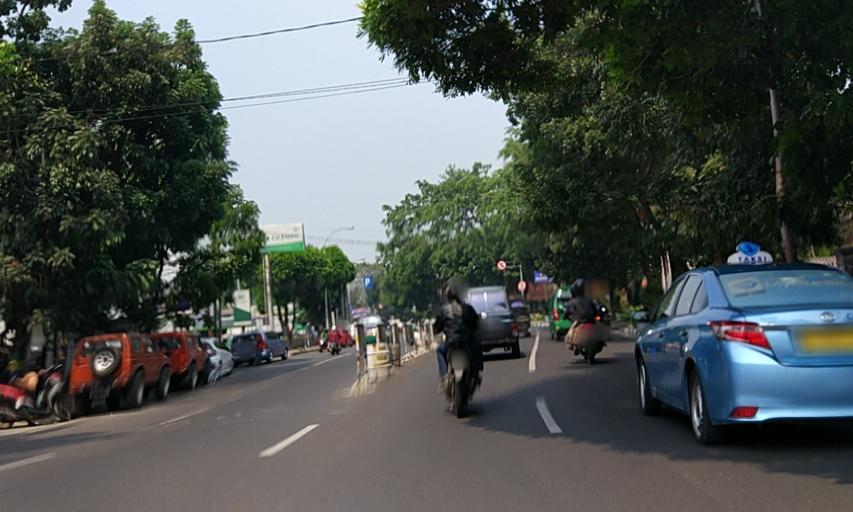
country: ID
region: West Java
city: Bandung
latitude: -6.9091
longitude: 107.6044
